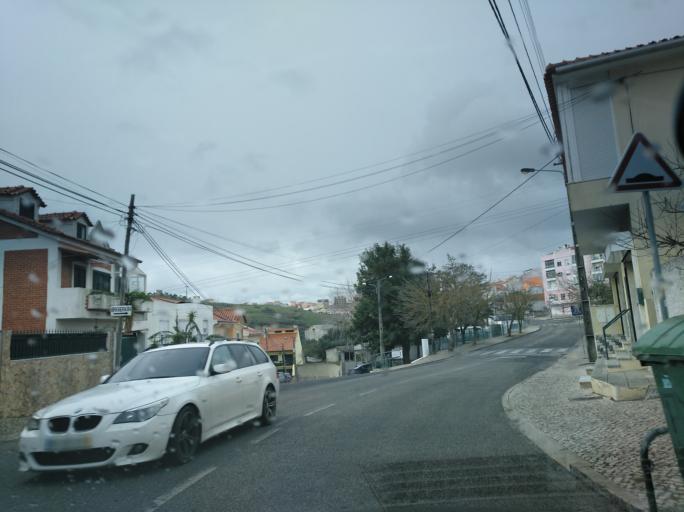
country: PT
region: Lisbon
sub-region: Odivelas
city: Famoes
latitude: 38.7938
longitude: -9.2200
